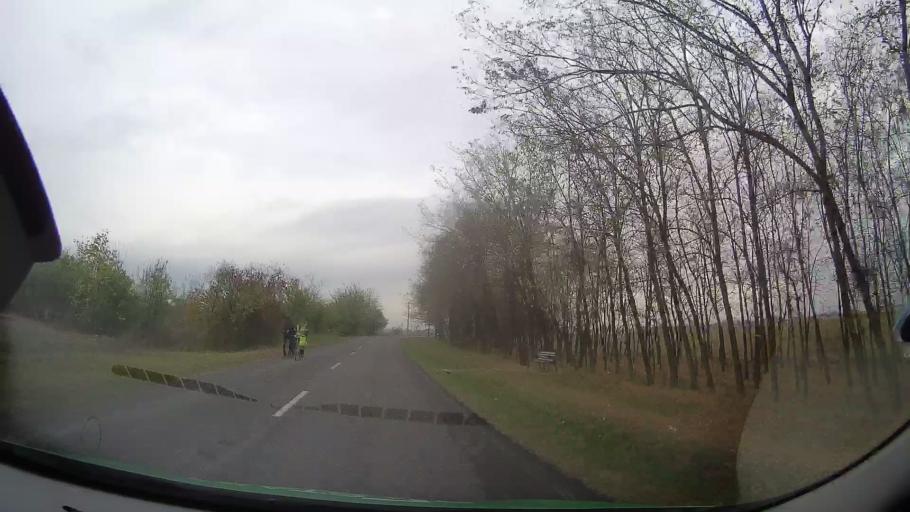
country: RO
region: Prahova
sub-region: Comuna Berceni
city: Berceni
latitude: 44.9389
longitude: 26.1127
